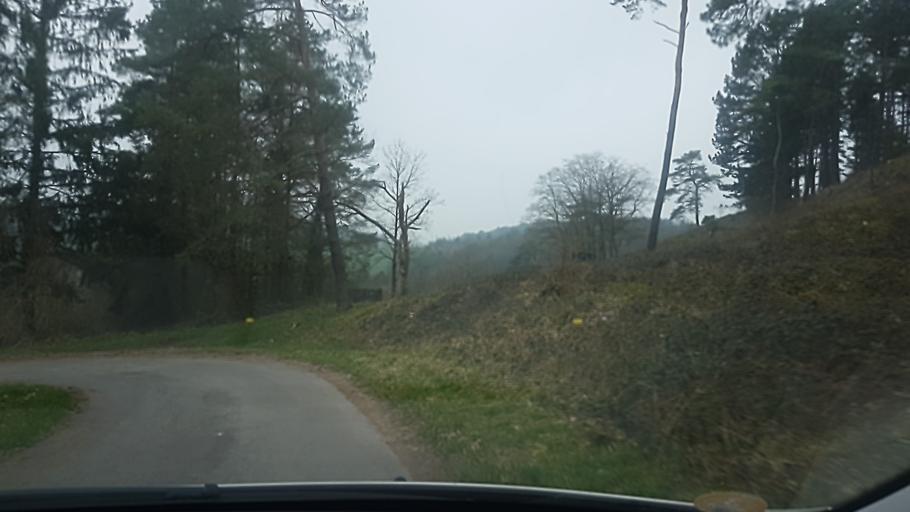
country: FR
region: Champagne-Ardenne
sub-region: Departement des Ardennes
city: Vireux-Molhain
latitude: 50.0847
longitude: 4.6307
